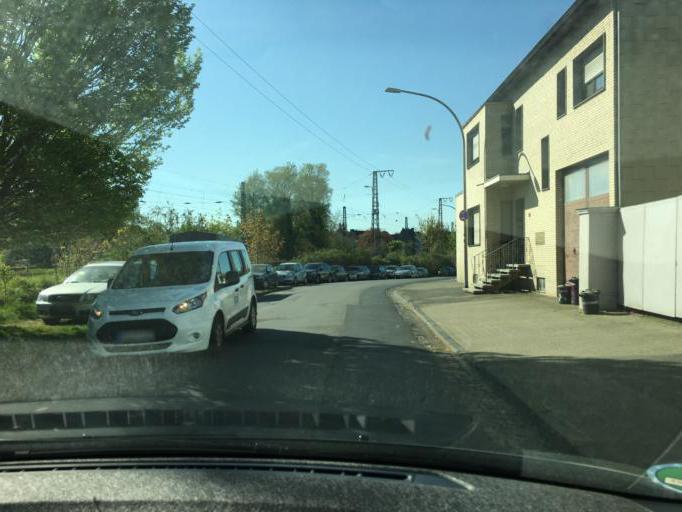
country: DE
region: North Rhine-Westphalia
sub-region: Regierungsbezirk Dusseldorf
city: Monchengladbach
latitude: 51.1602
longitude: 6.4387
